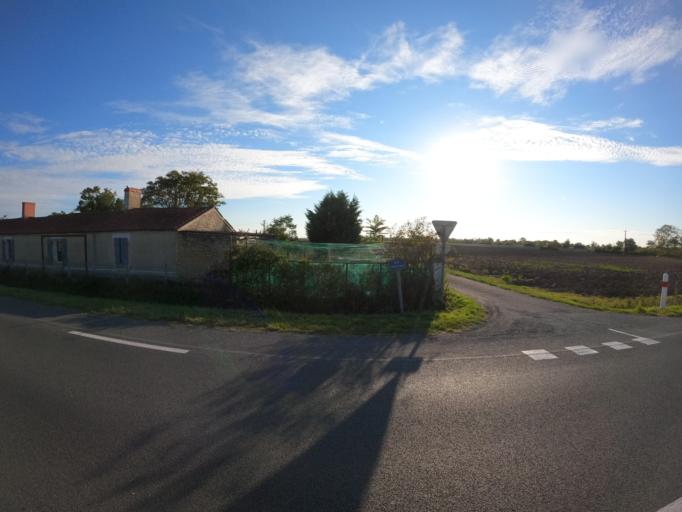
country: FR
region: Pays de la Loire
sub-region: Departement de la Vendee
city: Chaille-les-Marais
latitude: 46.3725
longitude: -1.0001
